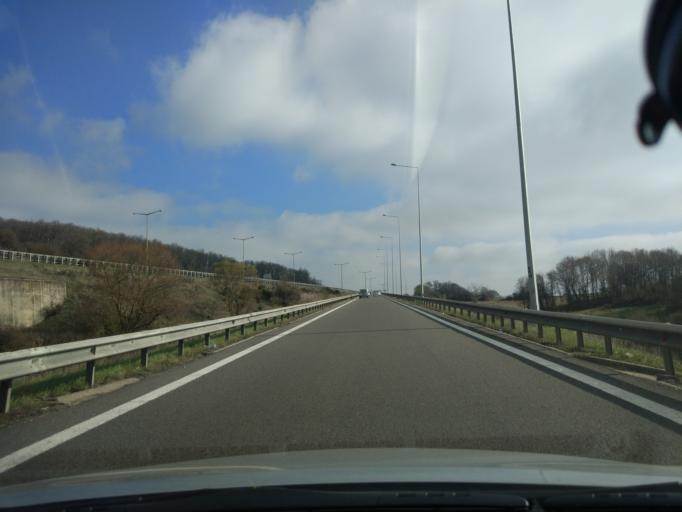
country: TR
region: Bolu
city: Bolu
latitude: 40.7206
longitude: 31.4811
